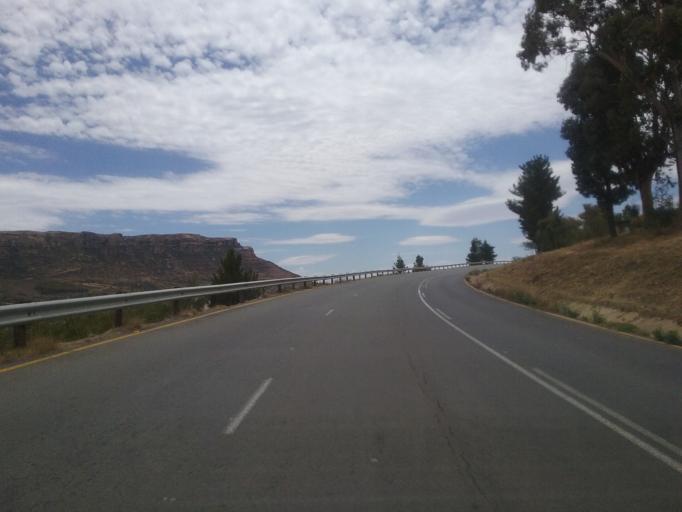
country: LS
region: Maseru
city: Maseru
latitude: -29.5118
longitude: 27.5232
